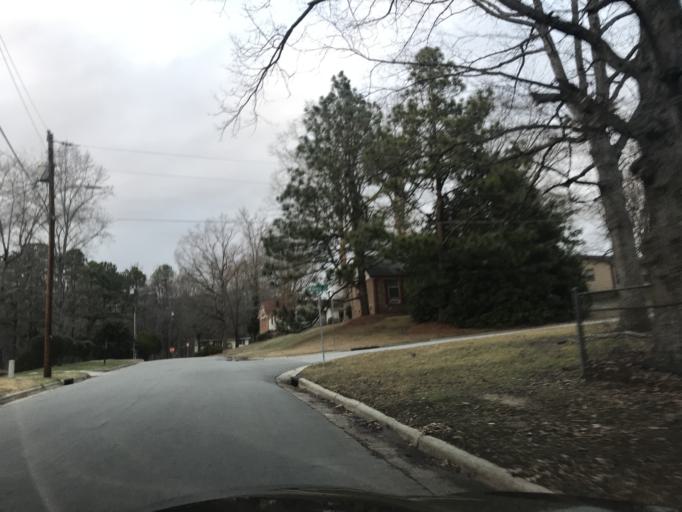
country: US
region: North Carolina
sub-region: Wake County
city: Garner
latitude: 35.7409
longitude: -78.6195
